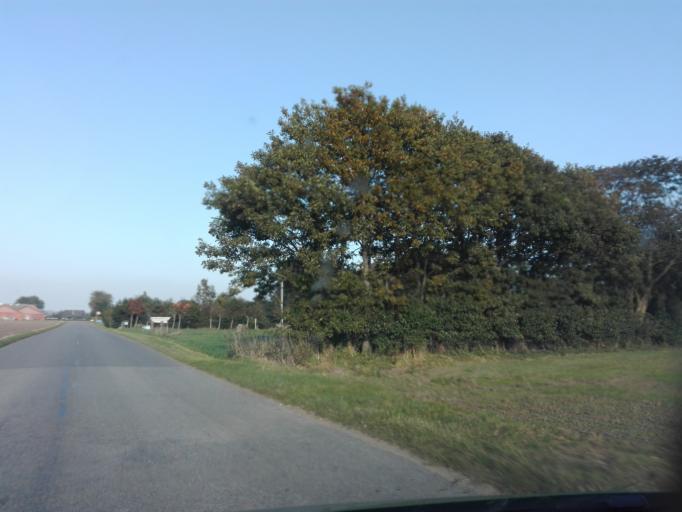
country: DK
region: Central Jutland
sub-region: Odder Kommune
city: Odder
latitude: 55.8945
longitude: 10.1985
